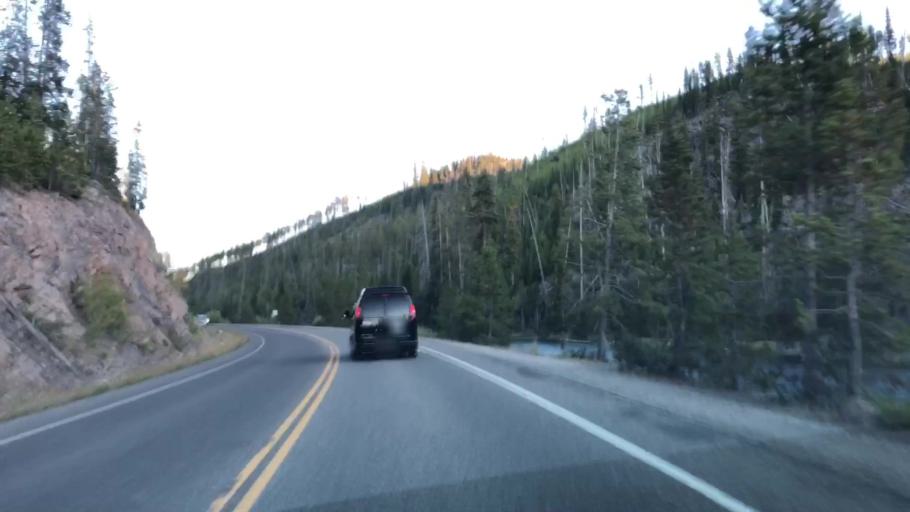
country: US
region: Montana
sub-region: Gallatin County
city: West Yellowstone
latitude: 44.6058
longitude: -110.8448
